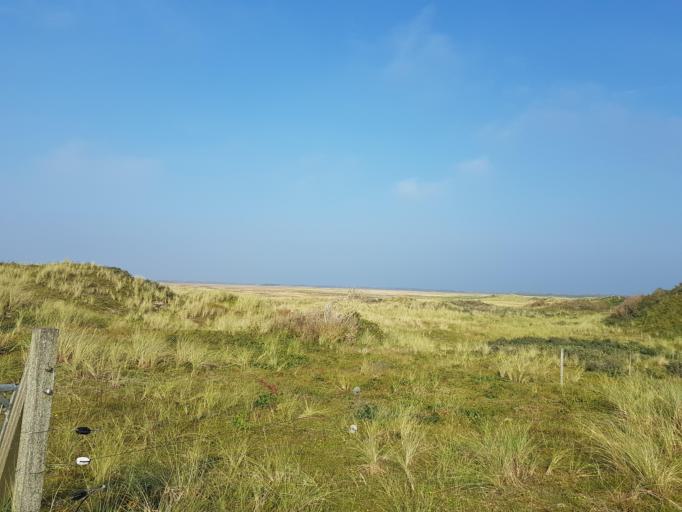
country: NL
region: North Holland
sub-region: Gemeente Texel
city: Den Burg
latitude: 53.1411
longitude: 4.8054
